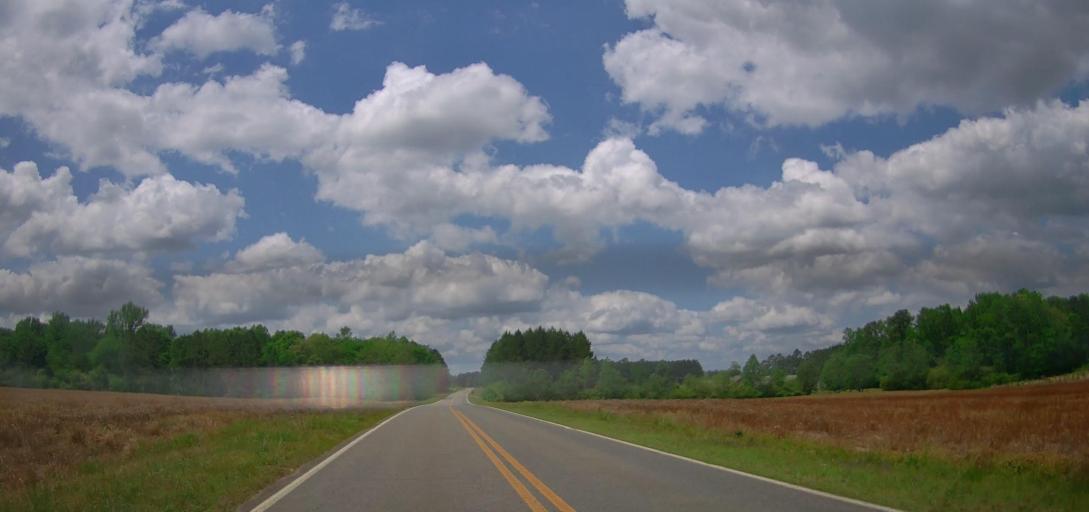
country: US
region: Georgia
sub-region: Laurens County
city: Dublin
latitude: 32.5997
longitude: -83.0019
